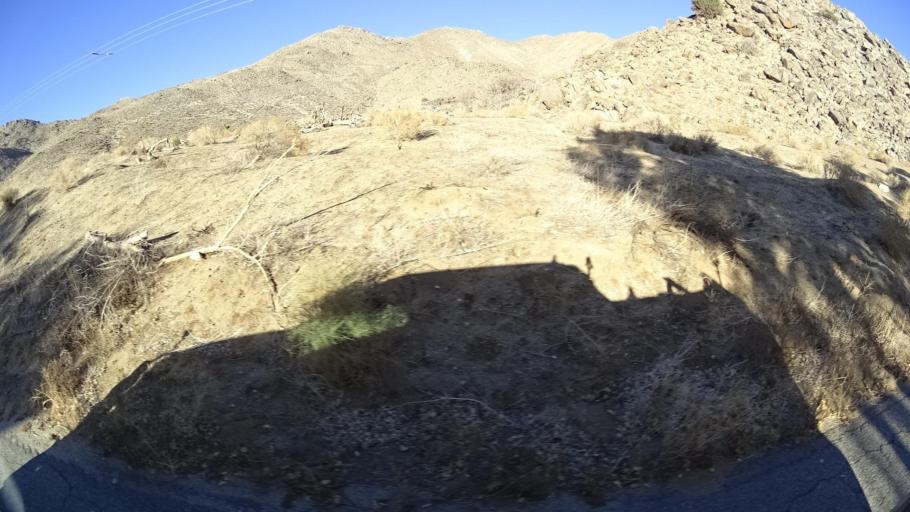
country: US
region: California
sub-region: Kern County
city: Weldon
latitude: 35.5624
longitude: -118.2393
